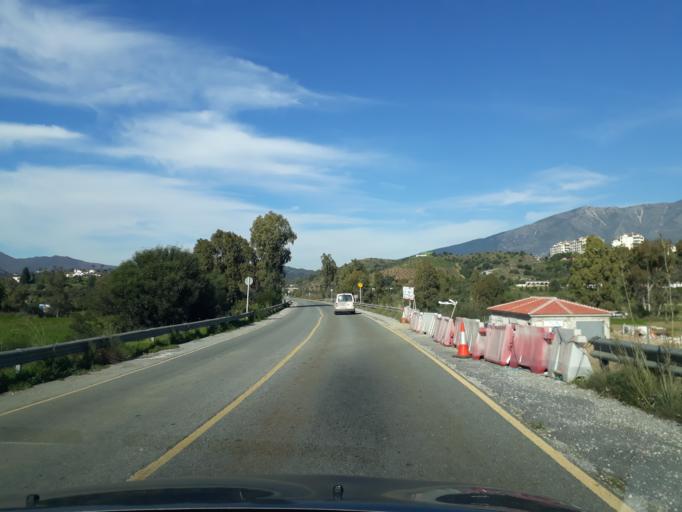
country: ES
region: Andalusia
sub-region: Provincia de Malaga
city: Fuengirola
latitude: 36.5426
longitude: -4.6872
